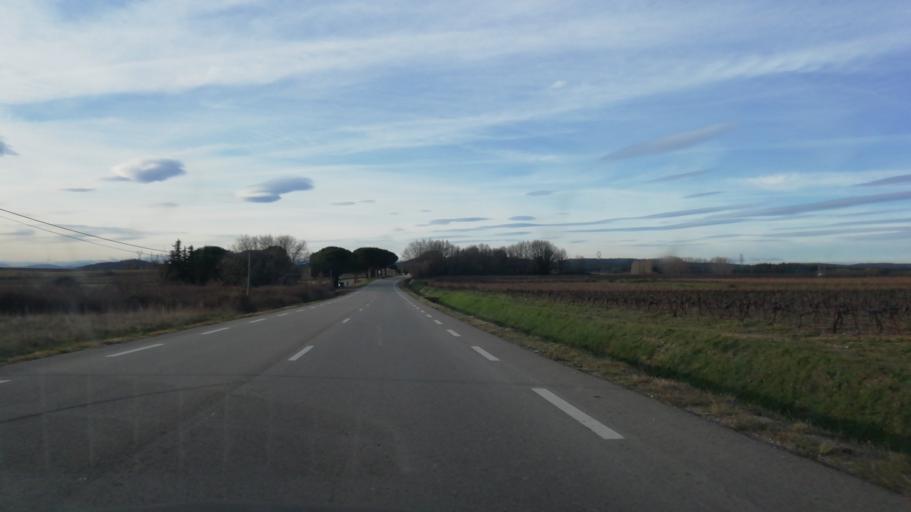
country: FR
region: Languedoc-Roussillon
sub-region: Departement du Gard
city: Saint-Mamert-du-Gard
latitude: 43.8572
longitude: 4.1734
